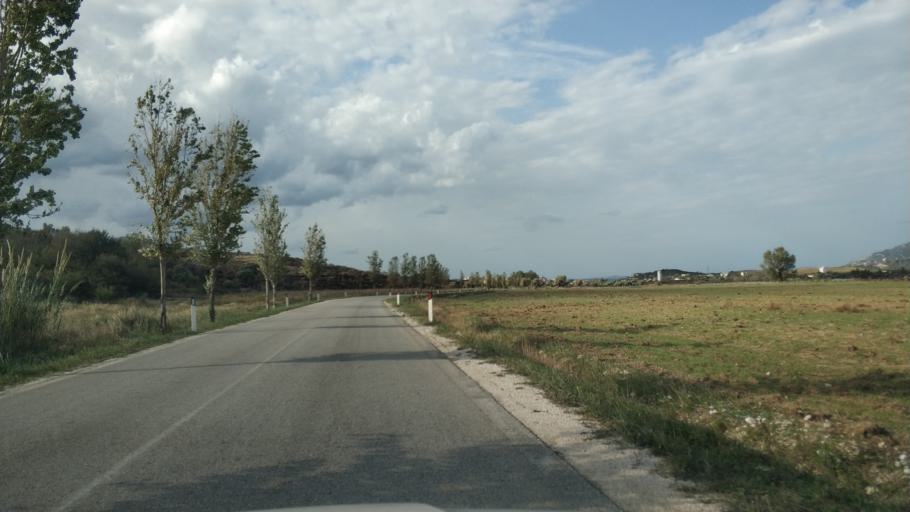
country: AL
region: Vlore
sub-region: Rrethi i Vlores
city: Orikum
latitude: 40.3152
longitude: 19.4855
